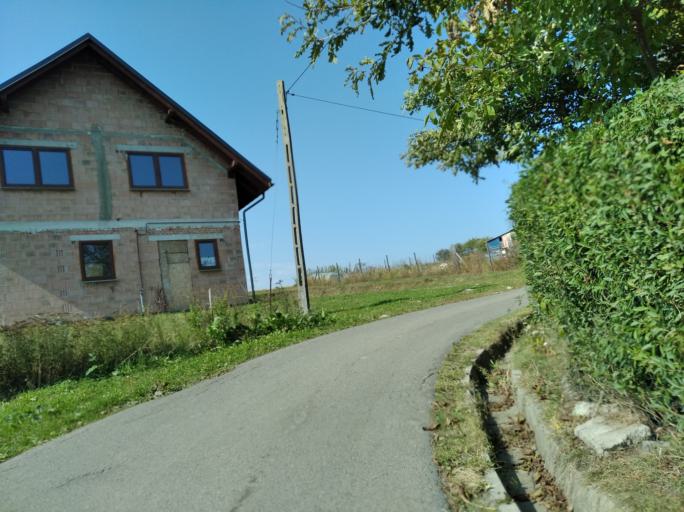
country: PL
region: Subcarpathian Voivodeship
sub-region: Powiat strzyzowski
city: Babica
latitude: 49.9391
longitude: 21.8591
